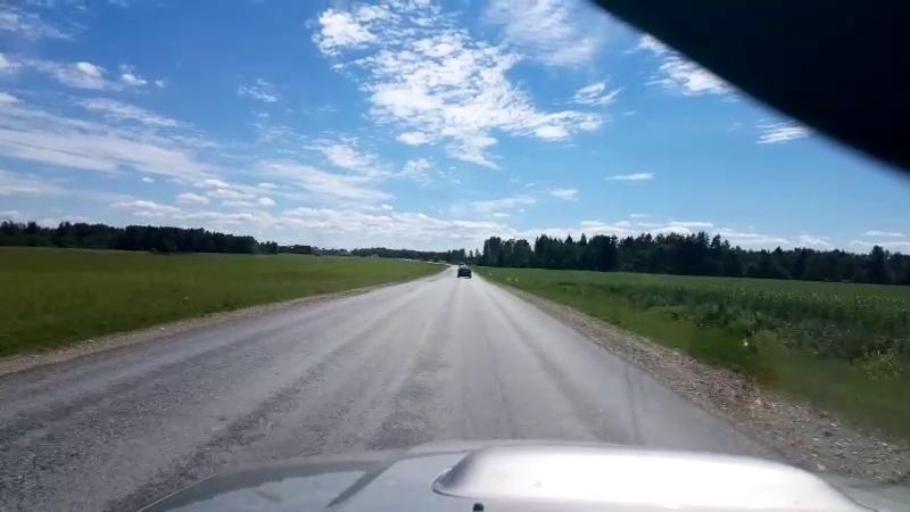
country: EE
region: Jogevamaa
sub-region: Jogeva linn
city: Jogeva
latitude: 58.8303
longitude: 26.2873
